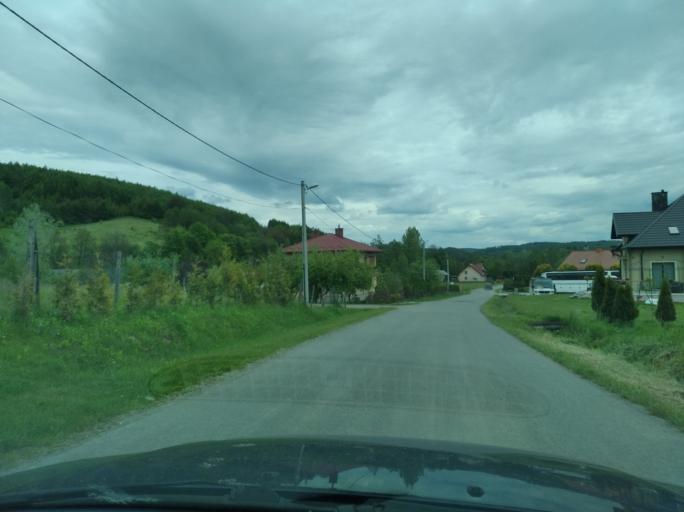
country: PL
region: Subcarpathian Voivodeship
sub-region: Powiat przemyski
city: Przedmiescie Dubieckie
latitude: 49.8327
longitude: 22.3237
